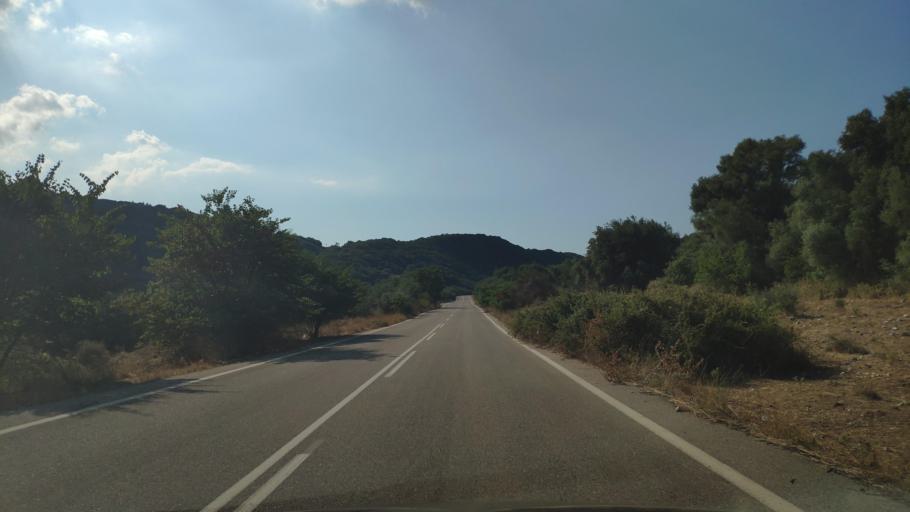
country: GR
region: West Greece
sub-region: Nomos Aitolias kai Akarnanias
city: Stanos
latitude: 38.7733
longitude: 21.1546
